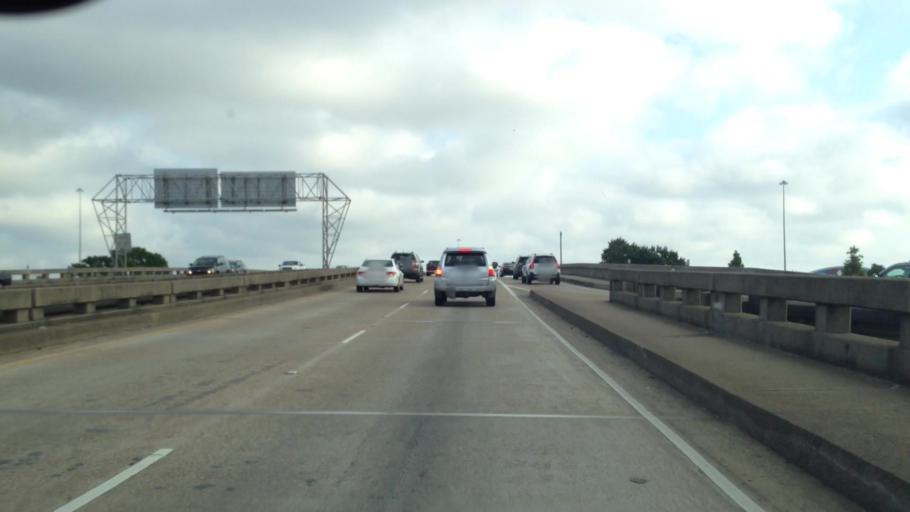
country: US
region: Louisiana
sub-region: Jefferson Parish
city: Metairie Terrace
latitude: 29.9975
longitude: -90.1839
